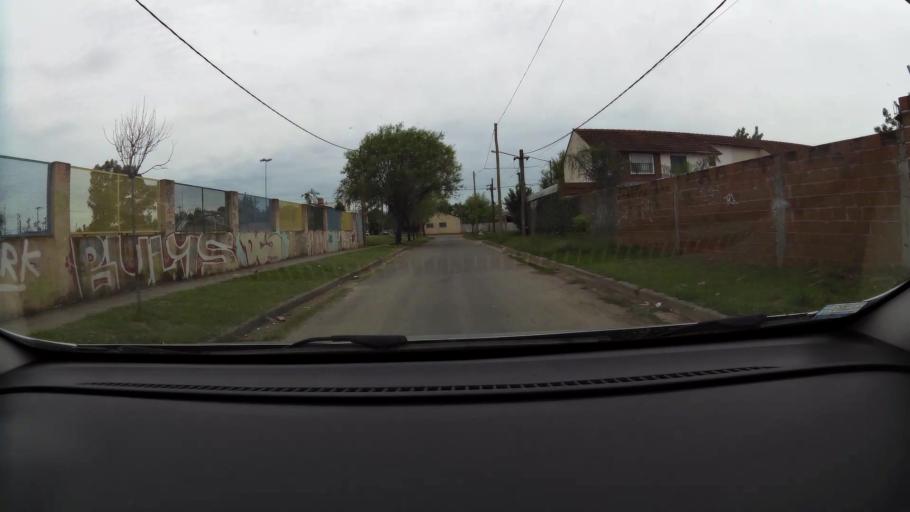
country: AR
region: Buenos Aires
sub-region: Partido de Campana
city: Campana
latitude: -34.2097
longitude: -58.9448
